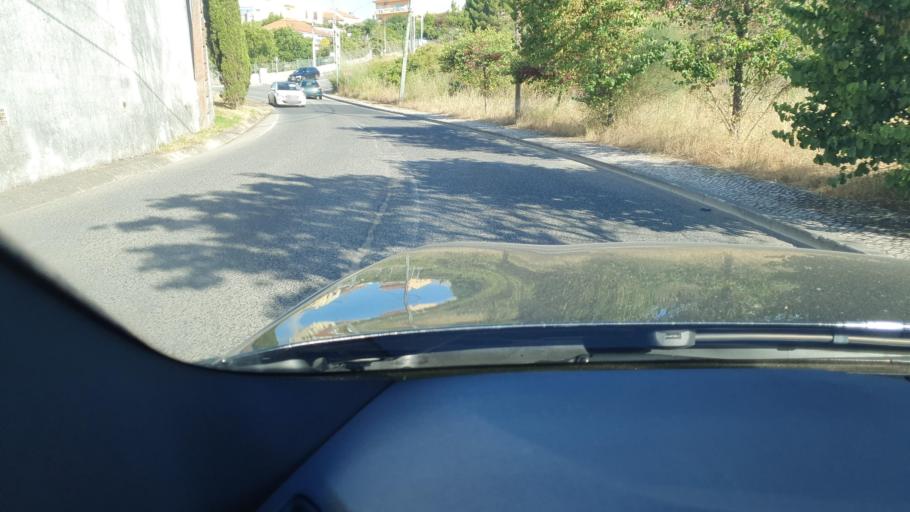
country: PT
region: Lisbon
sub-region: Sintra
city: Belas
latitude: 38.7961
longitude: -9.2474
